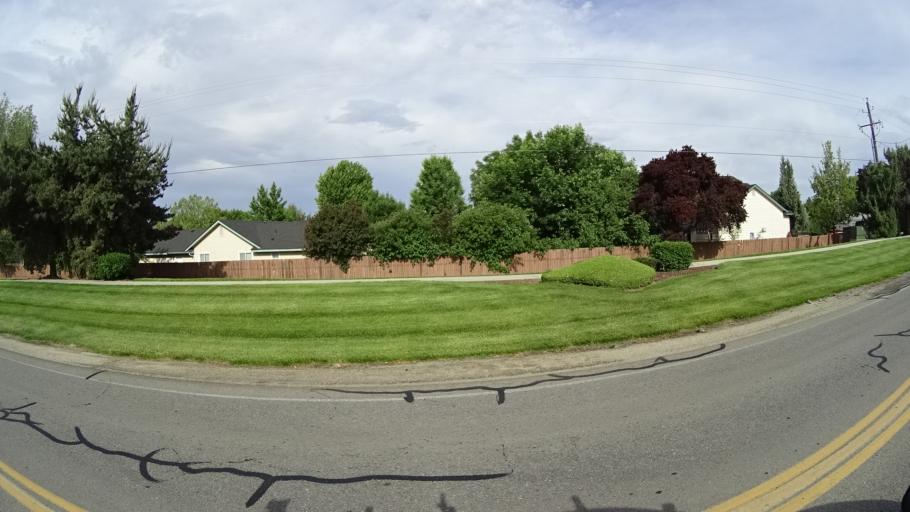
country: US
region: Idaho
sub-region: Ada County
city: Meridian
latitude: 43.5880
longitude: -116.3746
